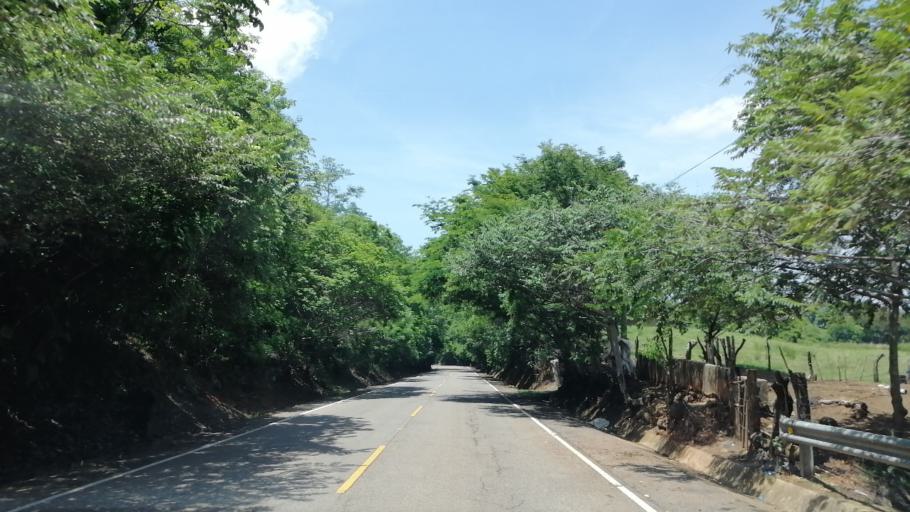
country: SV
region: Chalatenango
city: Nueva Concepcion
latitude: 14.1737
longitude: -89.3146
